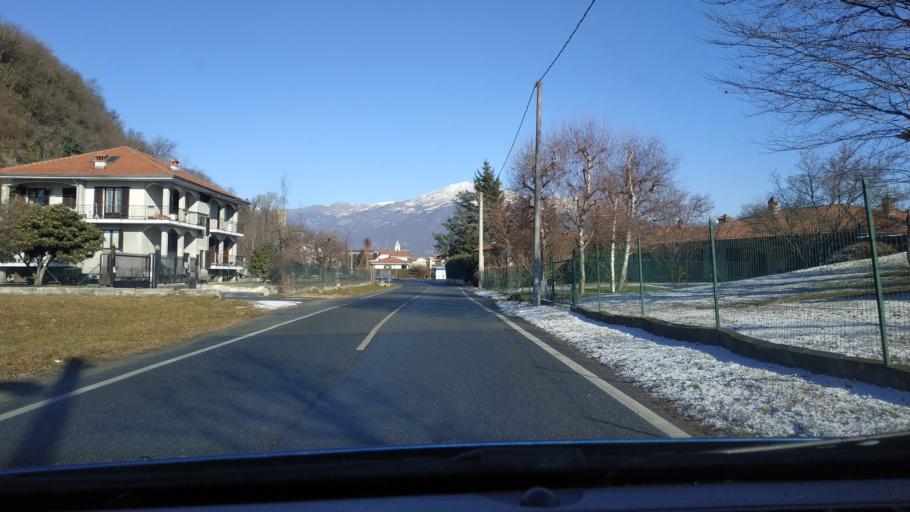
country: IT
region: Piedmont
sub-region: Provincia di Torino
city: Salerano Canavese
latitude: 45.4536
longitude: 7.8497
